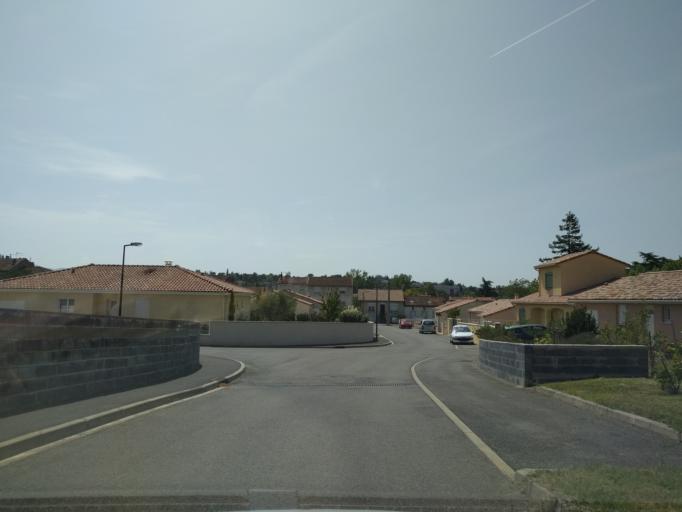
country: FR
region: Midi-Pyrenees
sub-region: Departement du Tarn
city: Castres
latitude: 43.5968
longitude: 2.2501
